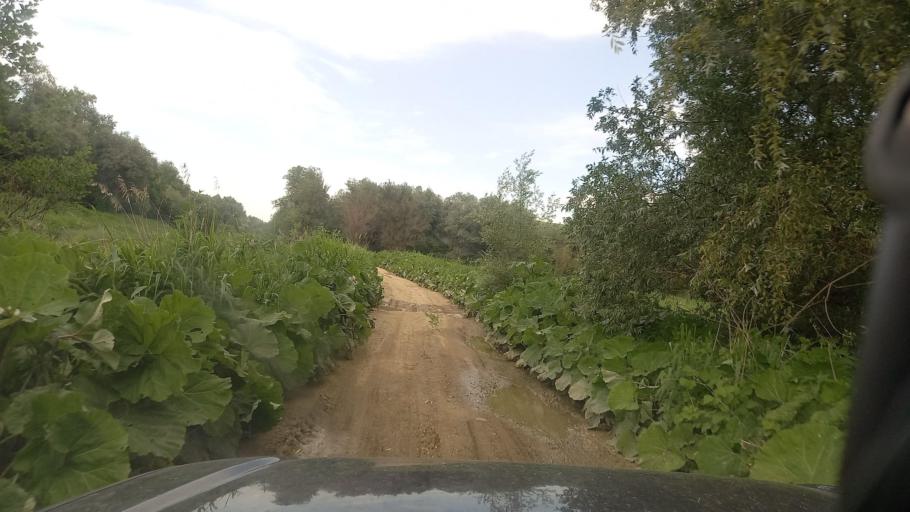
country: RU
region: Krasnodarskiy
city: Peredovaya
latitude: 44.0825
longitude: 41.3561
